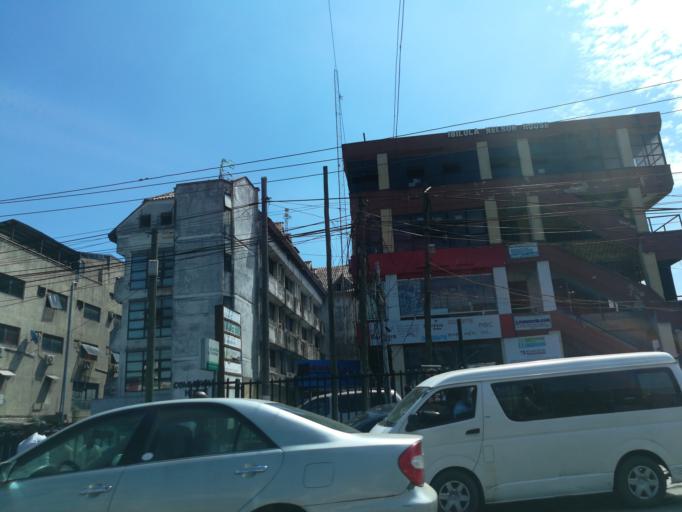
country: NG
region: Lagos
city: Ikeja
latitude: 6.6042
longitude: 3.3507
